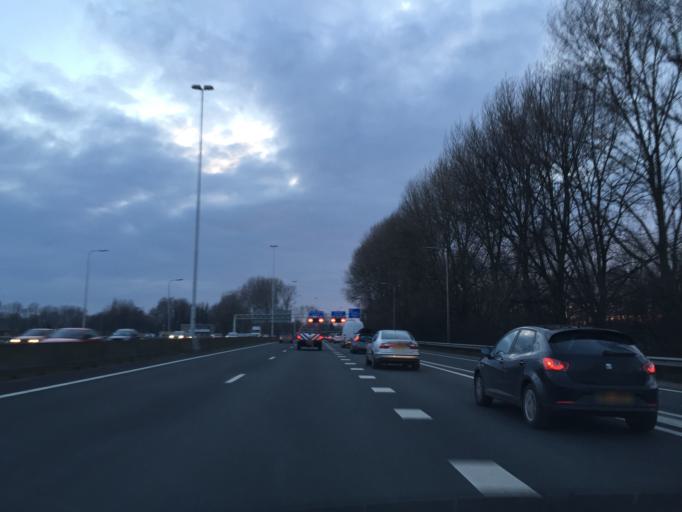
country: NL
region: South Holland
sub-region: Gemeente Rotterdam
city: Rotterdam
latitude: 51.9370
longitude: 4.4570
